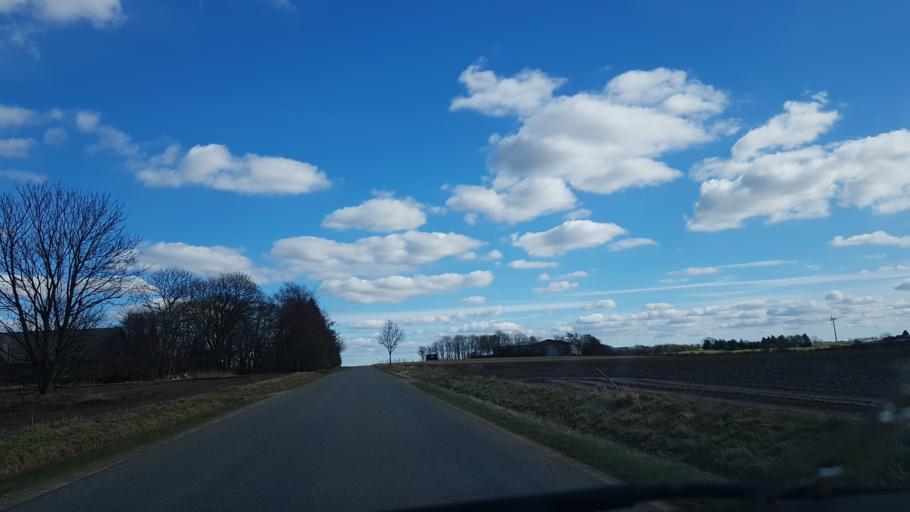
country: DK
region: South Denmark
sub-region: Vejen Kommune
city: Brorup
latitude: 55.4056
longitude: 8.9440
